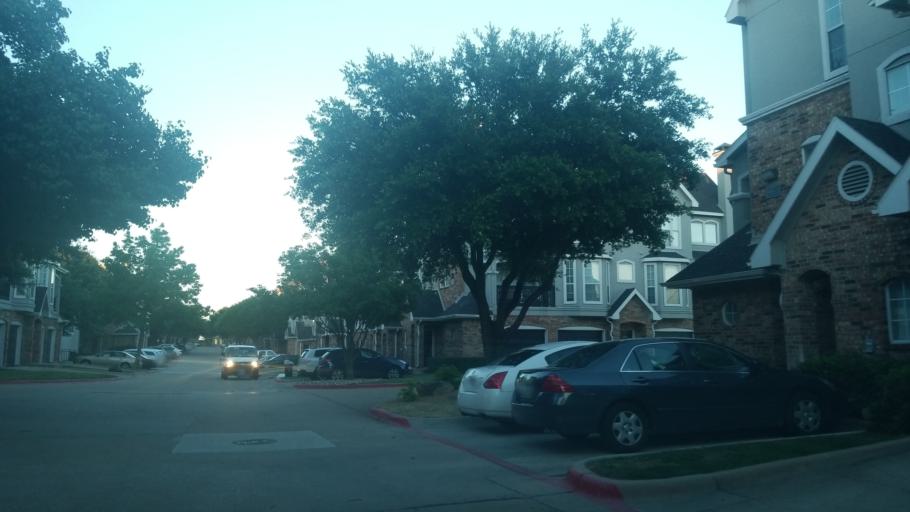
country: US
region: Texas
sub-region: Dallas County
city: Irving
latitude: 32.8757
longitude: -96.9661
